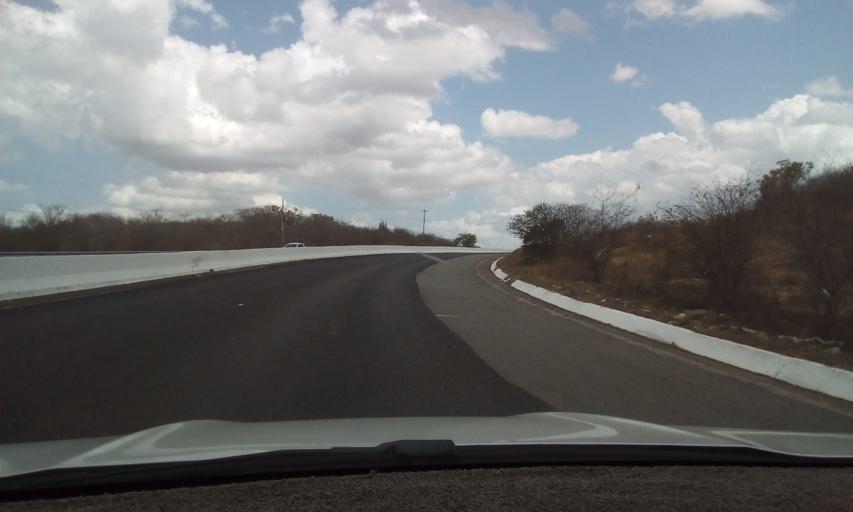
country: BR
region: Pernambuco
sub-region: Toritama
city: Toritama
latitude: -8.1217
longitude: -35.9964
